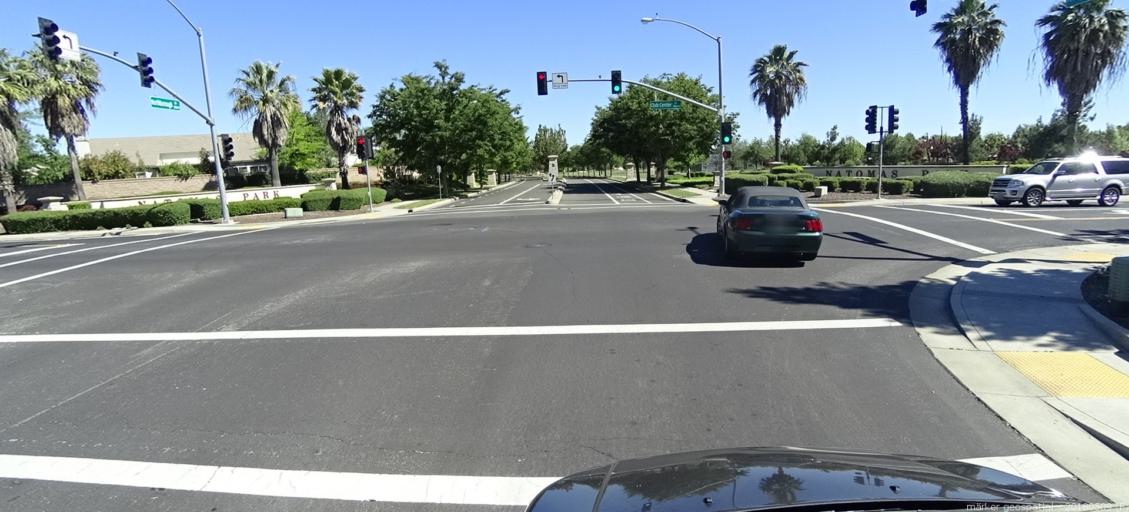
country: US
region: California
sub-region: Sacramento County
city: Elverta
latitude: 38.6728
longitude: -121.5191
